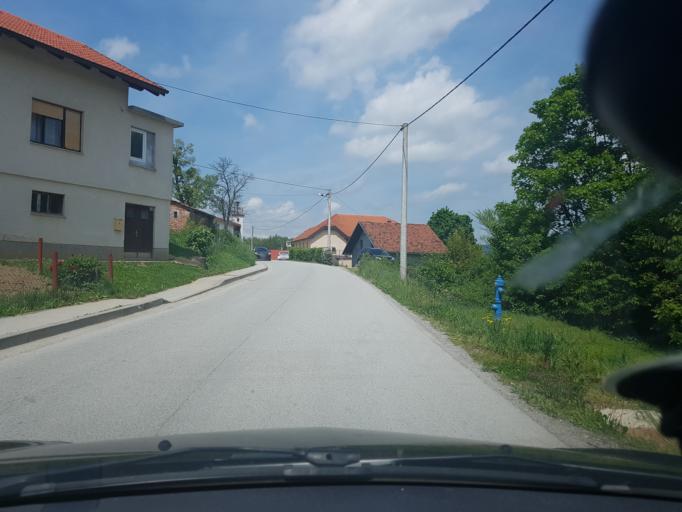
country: SI
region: Rogatec
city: Rogatec
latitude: 46.2084
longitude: 15.7277
